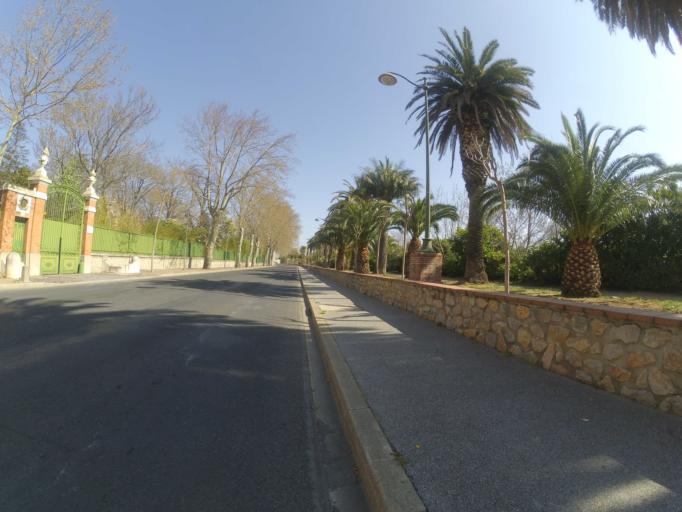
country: FR
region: Languedoc-Roussillon
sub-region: Departement des Pyrenees-Orientales
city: Thuir
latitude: 42.6357
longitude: 2.7589
